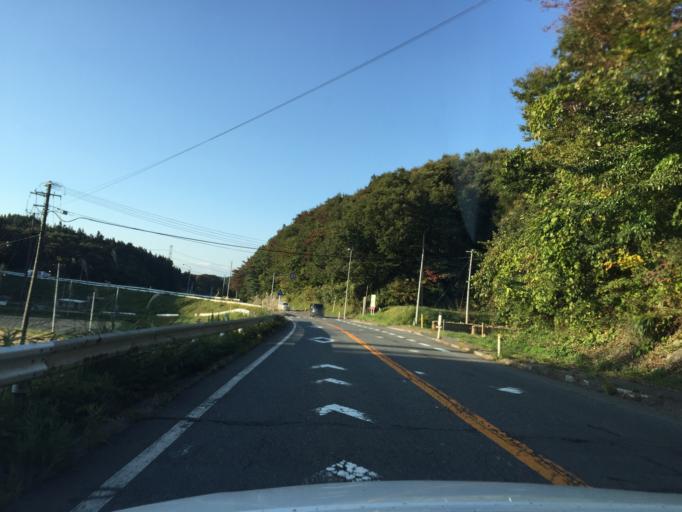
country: JP
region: Fukushima
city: Ishikawa
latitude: 37.1897
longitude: 140.6428
